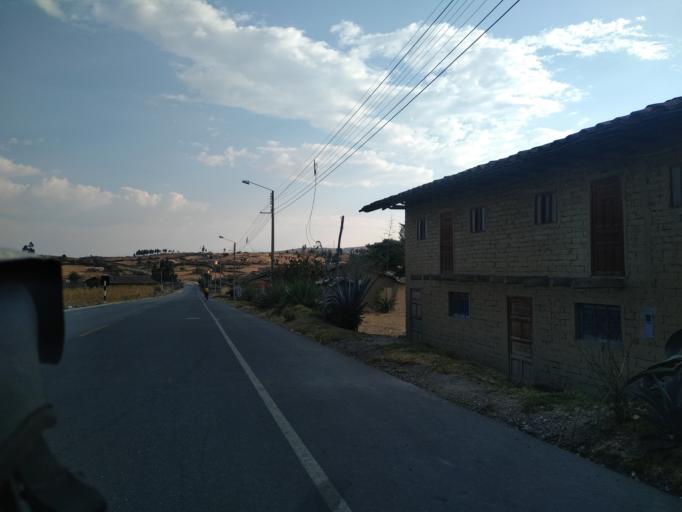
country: PE
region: Cajamarca
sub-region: San Marcos
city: La Grama
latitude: -7.3933
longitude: -78.1240
